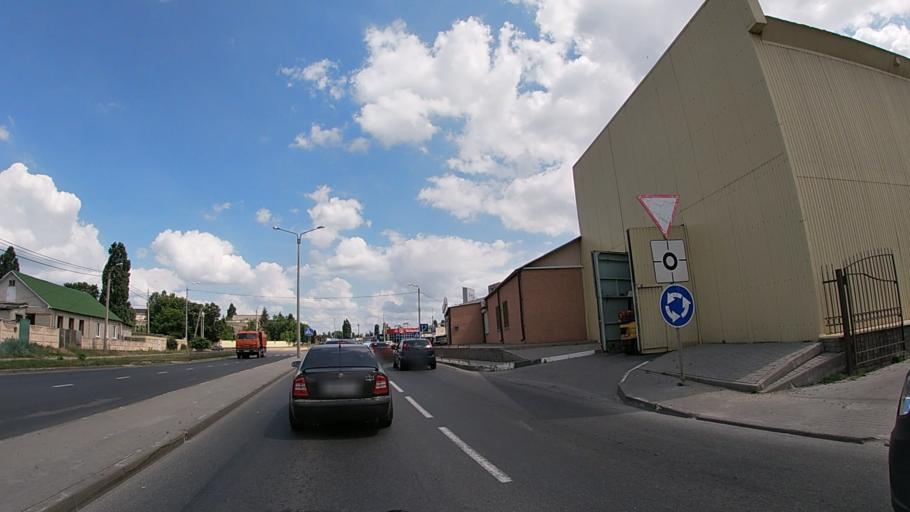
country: RU
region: Belgorod
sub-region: Belgorodskiy Rayon
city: Belgorod
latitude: 50.6122
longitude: 36.5346
